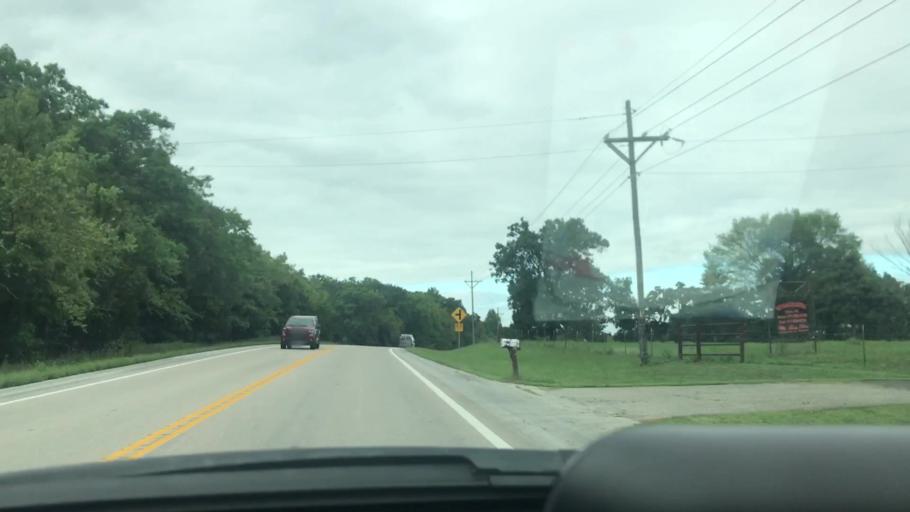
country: US
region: Missouri
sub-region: Hickory County
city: Hermitage
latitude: 37.8701
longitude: -93.1804
